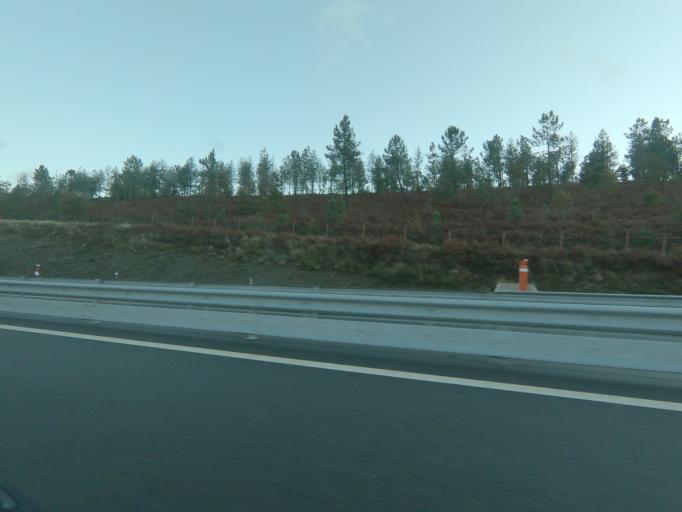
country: PT
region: Vila Real
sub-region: Santa Marta de Penaguiao
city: Santa Marta de Penaguiao
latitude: 41.2794
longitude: -7.8469
